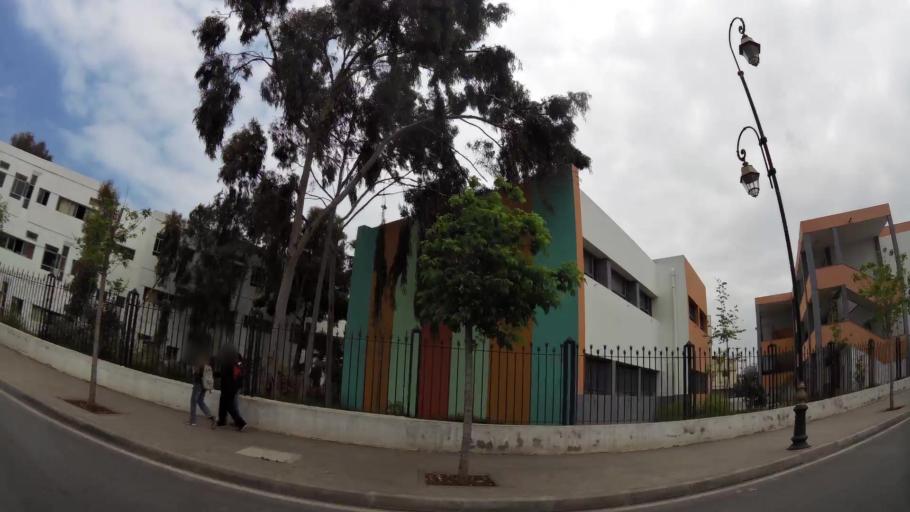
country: MA
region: Rabat-Sale-Zemmour-Zaer
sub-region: Skhirate-Temara
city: Temara
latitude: 33.9747
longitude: -6.8837
